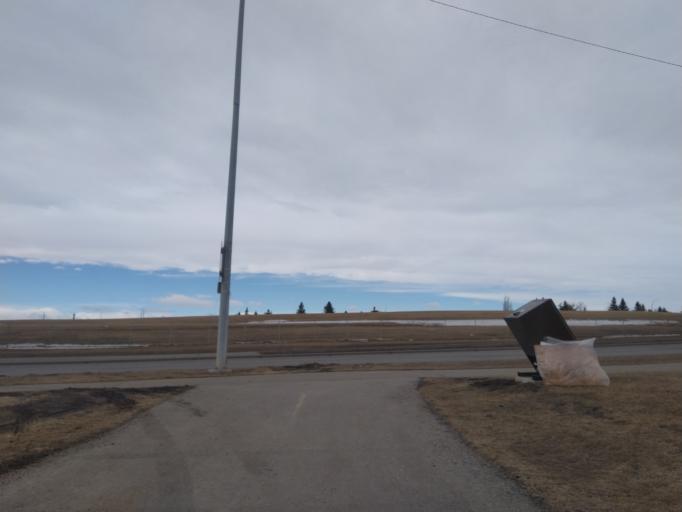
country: CA
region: Alberta
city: Chestermere
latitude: 51.0972
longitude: -113.9347
